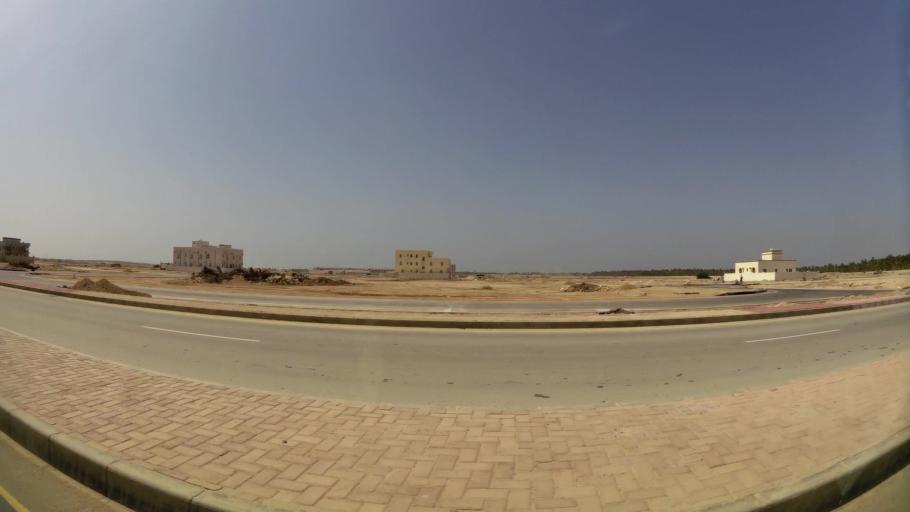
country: OM
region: Zufar
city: Salalah
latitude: 17.0393
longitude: 54.1222
